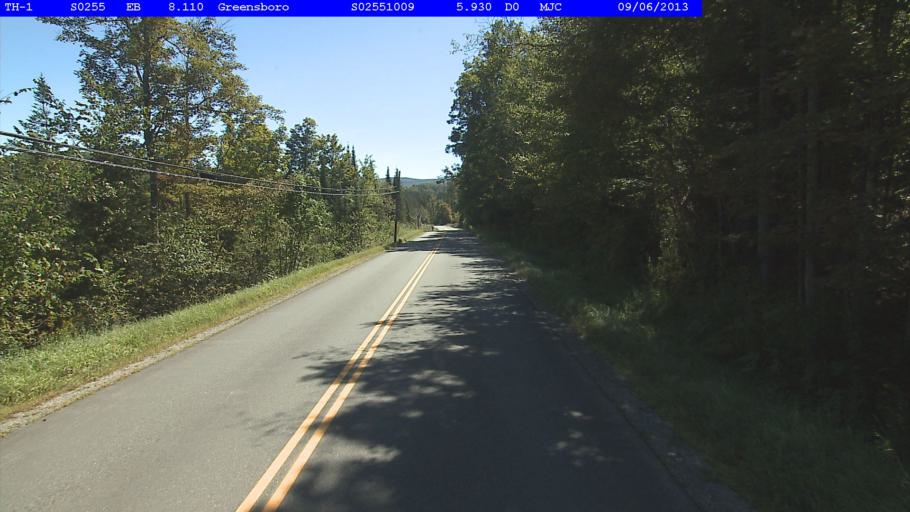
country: US
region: Vermont
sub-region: Caledonia County
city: Hardwick
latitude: 44.5664
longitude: -72.2858
